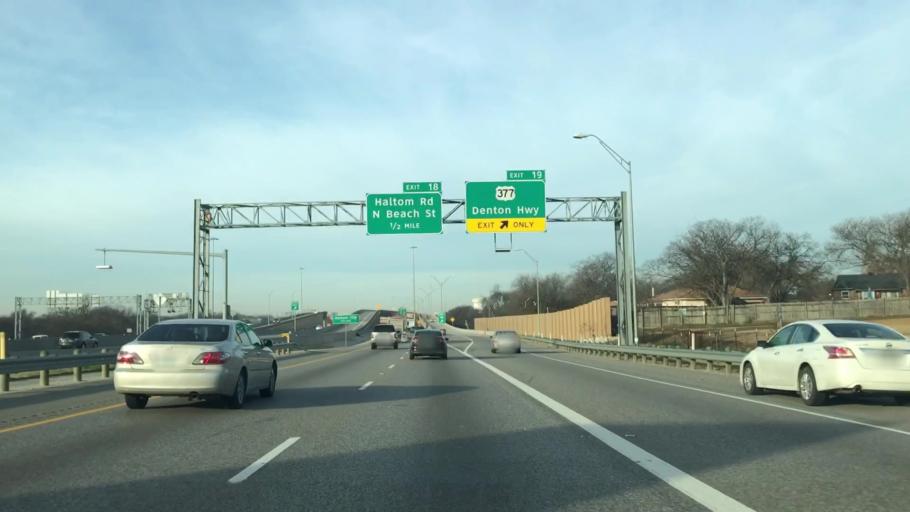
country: US
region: Texas
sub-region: Tarrant County
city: Watauga
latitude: 32.8405
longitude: -97.2546
